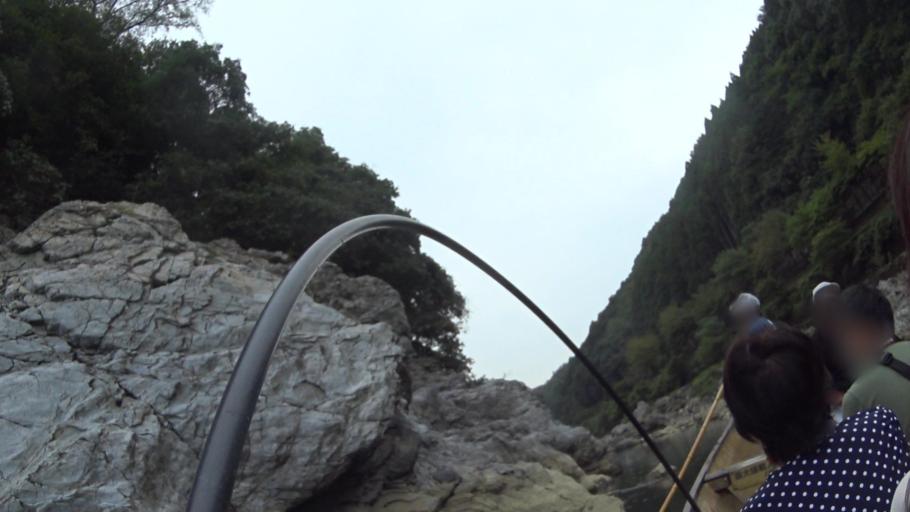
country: JP
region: Kyoto
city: Kameoka
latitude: 35.0237
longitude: 135.6422
